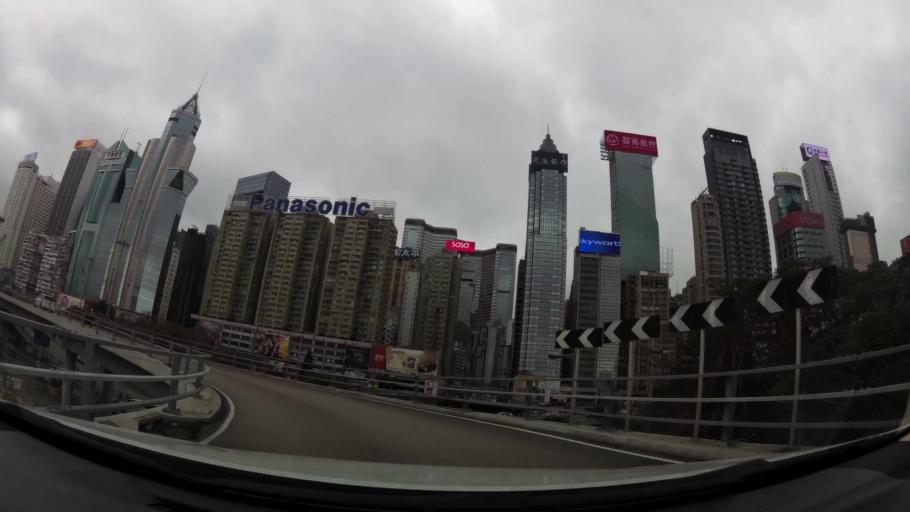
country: HK
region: Wanchai
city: Wan Chai
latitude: 22.2825
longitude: 114.1795
